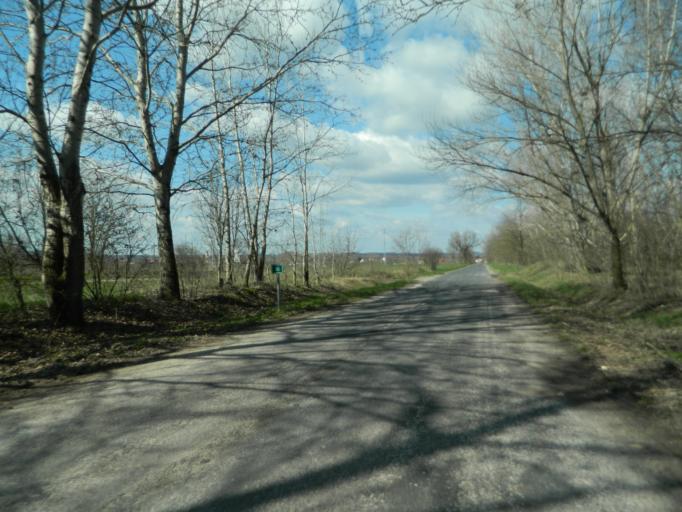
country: HU
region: Fejer
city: Szabadbattyan
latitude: 47.1237
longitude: 18.3910
